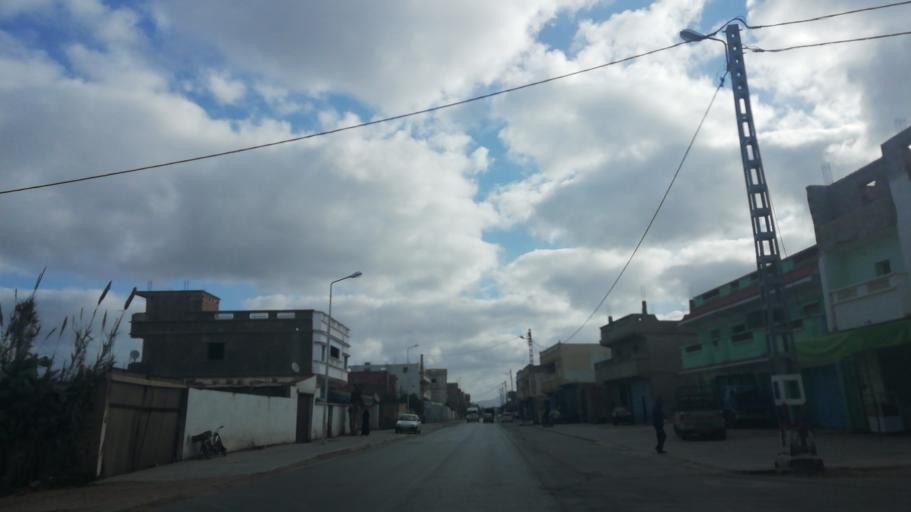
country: DZ
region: Relizane
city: Mazouna
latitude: 36.2596
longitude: 0.6042
